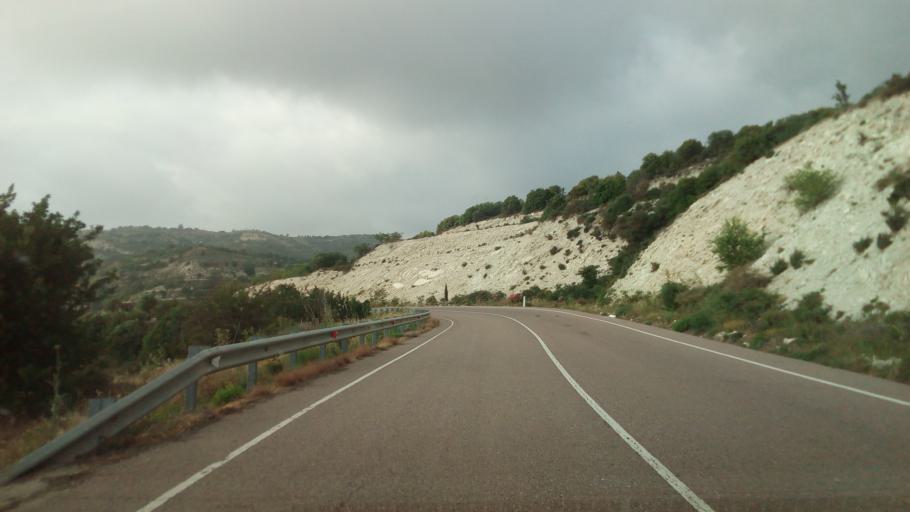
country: CY
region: Limassol
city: Pachna
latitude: 34.8301
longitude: 32.6850
